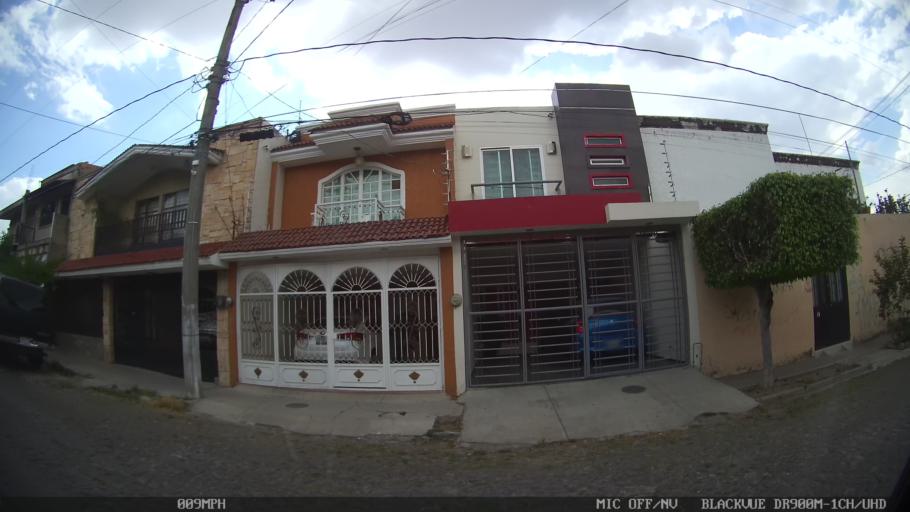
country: MX
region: Jalisco
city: Tlaquepaque
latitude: 20.6324
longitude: -103.2779
